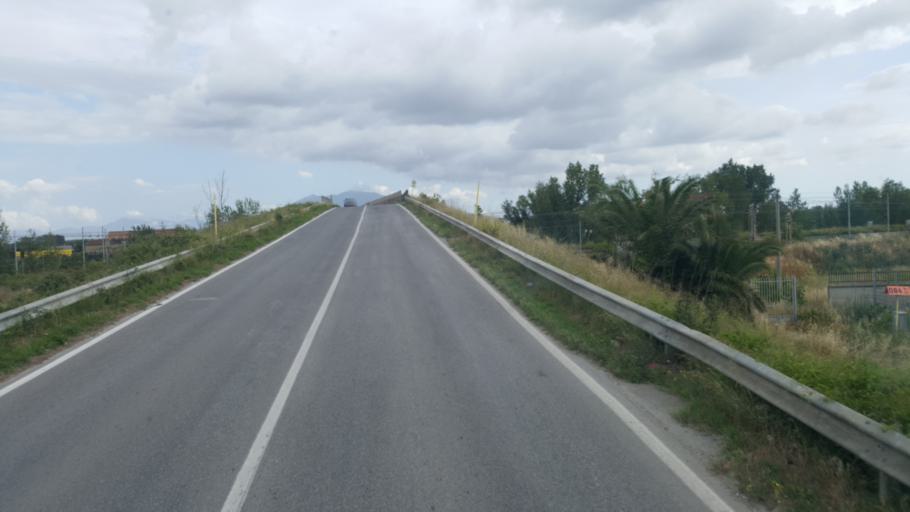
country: IT
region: Campania
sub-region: Provincia di Caserta
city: Maddaloni
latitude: 41.0043
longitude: 14.3931
